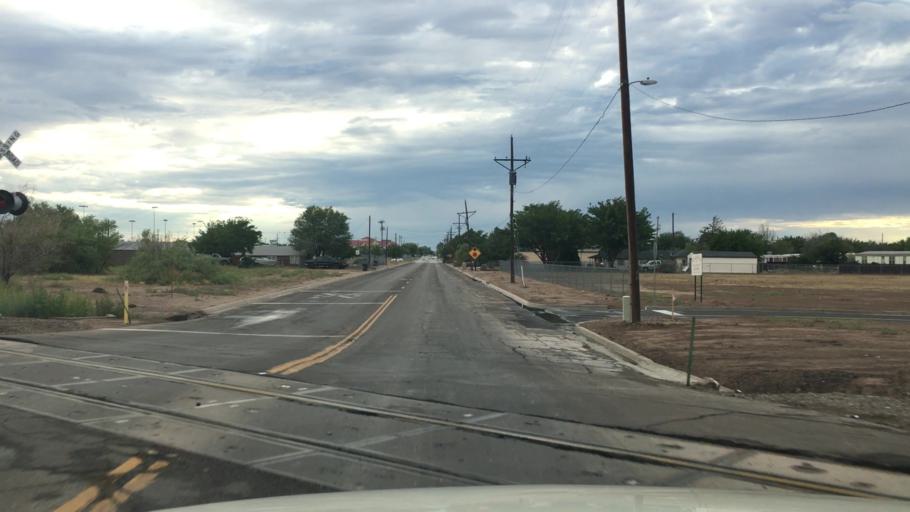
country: US
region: New Mexico
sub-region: Chaves County
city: Roswell
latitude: 33.4160
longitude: -104.5106
